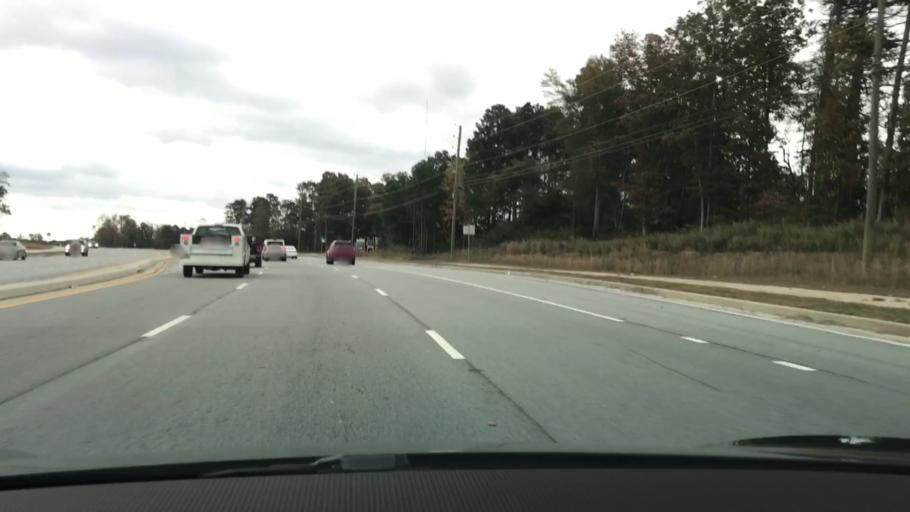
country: US
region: Georgia
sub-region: Hall County
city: Flowery Branch
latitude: 34.1351
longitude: -83.9441
